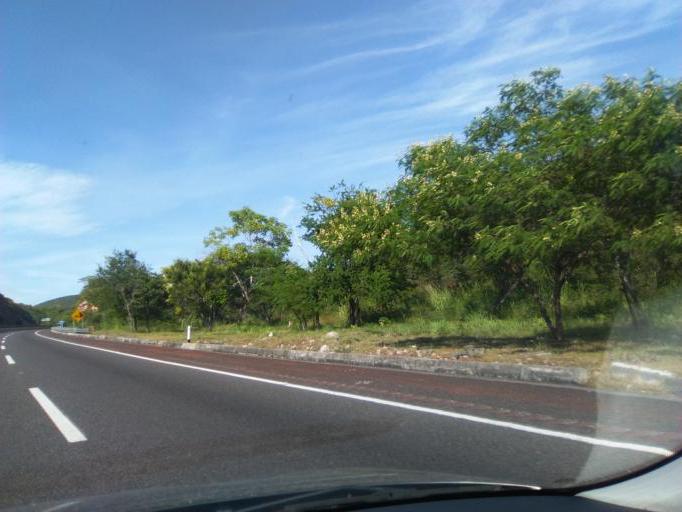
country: MX
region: Guerrero
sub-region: Huitzuco de los Figueroa
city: Ciudad de Huitzuco
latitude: 18.1563
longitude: -99.2130
